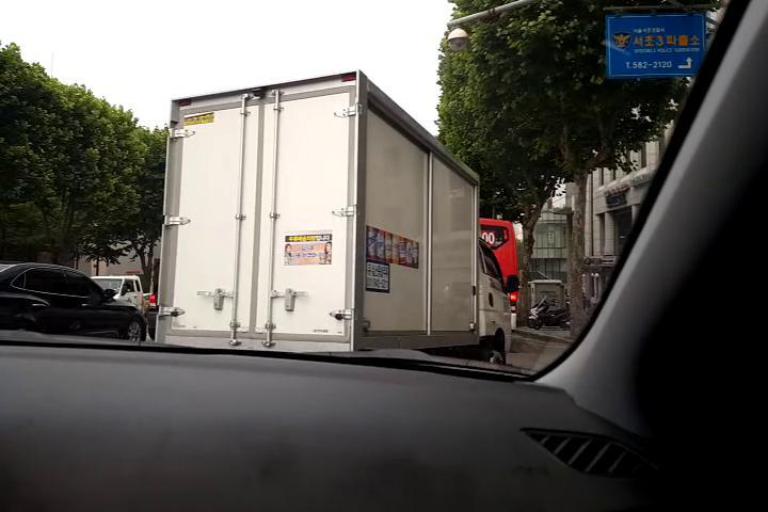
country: KR
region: Seoul
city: Seoul
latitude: 37.4920
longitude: 127.0083
